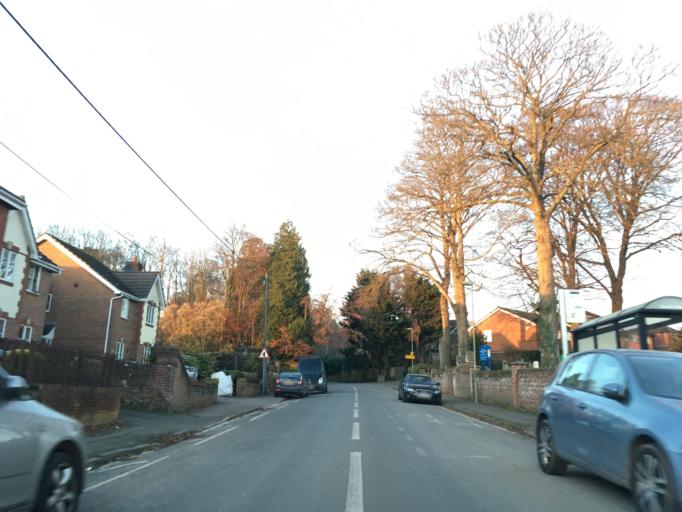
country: GB
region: England
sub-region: Hampshire
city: Bishopstoke
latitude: 50.9756
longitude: -1.3362
